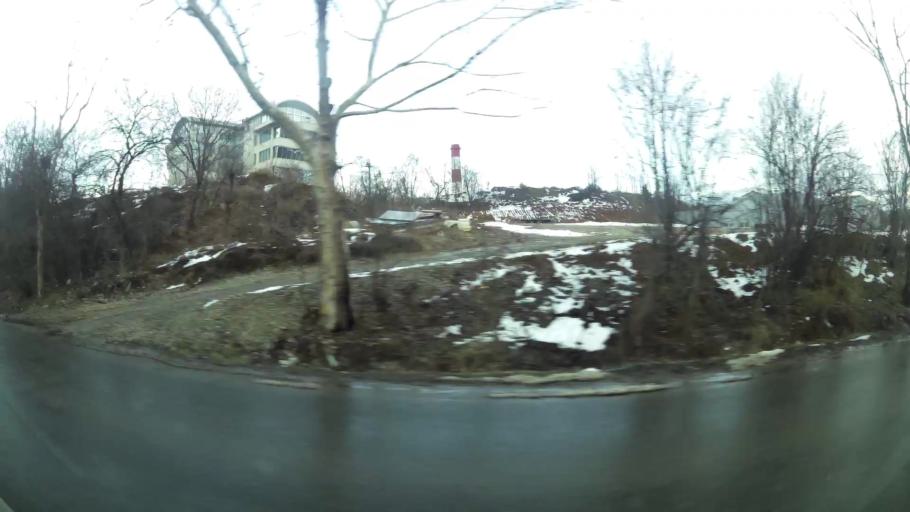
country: RS
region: Central Serbia
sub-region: Belgrade
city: Vozdovac
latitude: 44.7547
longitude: 20.4817
